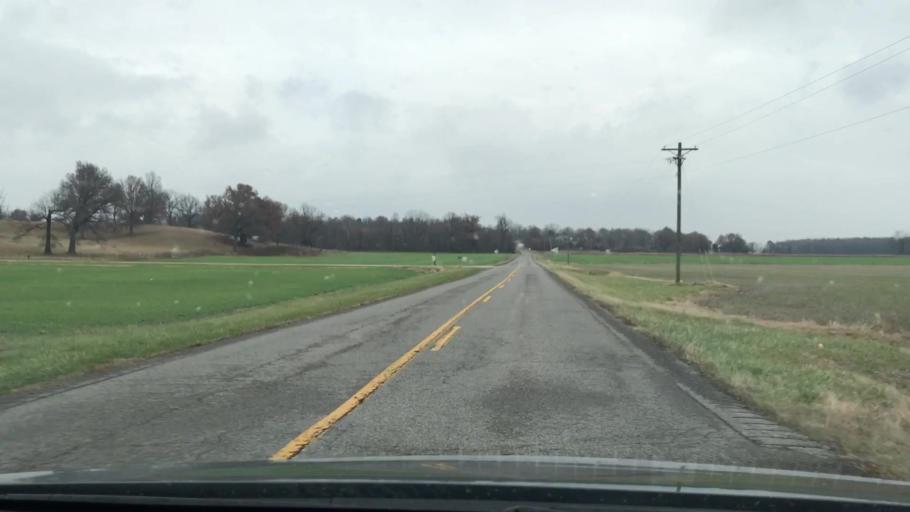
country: US
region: Kentucky
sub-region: McLean County
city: Calhoun
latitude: 37.5155
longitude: -87.4002
